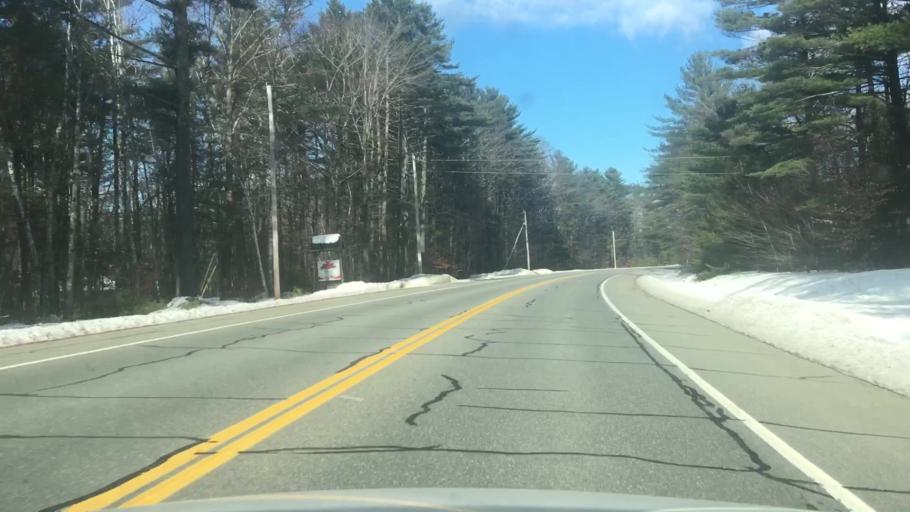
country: US
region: Maine
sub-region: Somerset County
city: Madison
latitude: 44.9809
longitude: -69.8673
